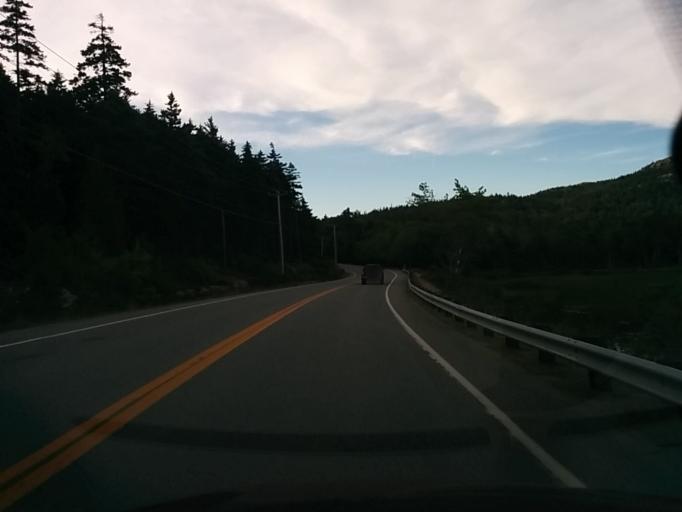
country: US
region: Maine
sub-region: Hancock County
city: Tremont
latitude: 44.3227
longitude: -68.2900
